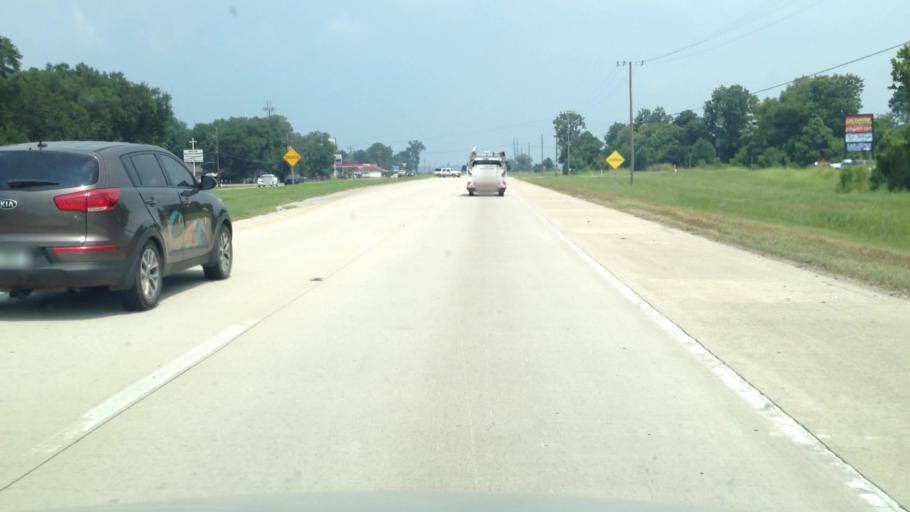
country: US
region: Louisiana
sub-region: West Baton Rouge Parish
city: Erwinville
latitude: 30.5008
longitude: -91.3120
